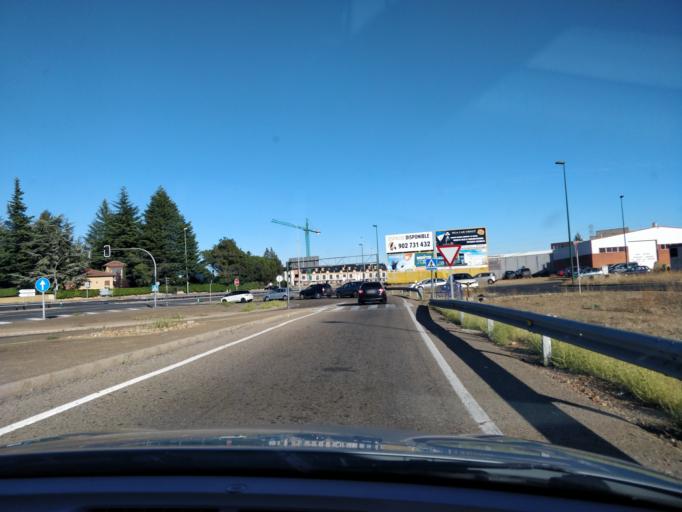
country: ES
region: Castille and Leon
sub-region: Provincia de Leon
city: San Andres del Rabanedo
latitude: 42.5909
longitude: -5.6137
